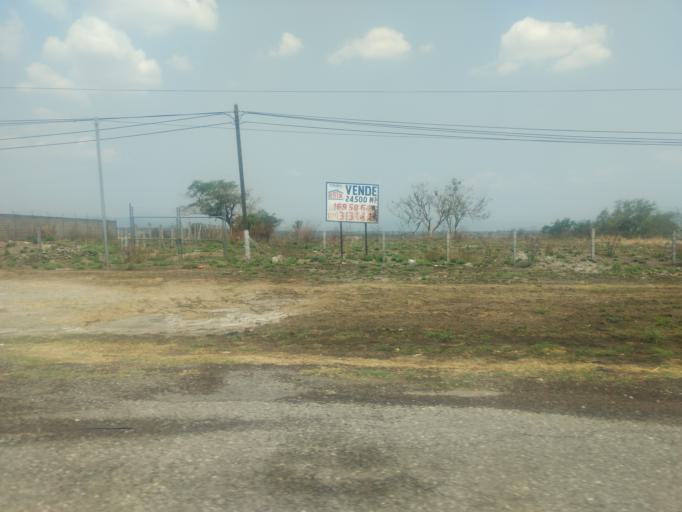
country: MX
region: Morelos
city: Ahuehuetzingo
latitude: 18.6895
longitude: -99.2846
